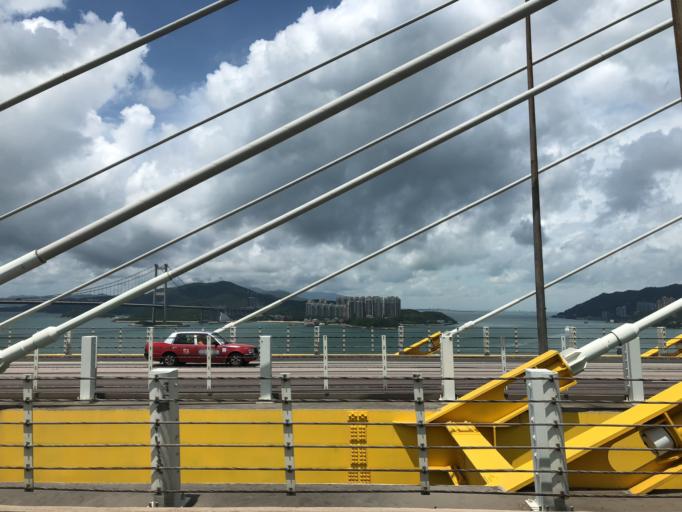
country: HK
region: Tsuen Wan
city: Tsuen Wan
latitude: 22.3625
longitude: 114.0806
